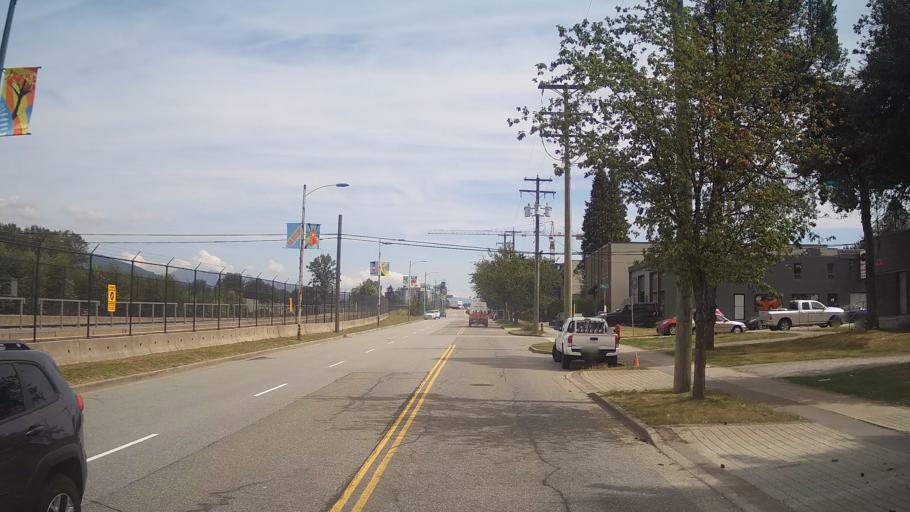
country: CA
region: British Columbia
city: Port Moody
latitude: 49.2777
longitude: -122.8554
